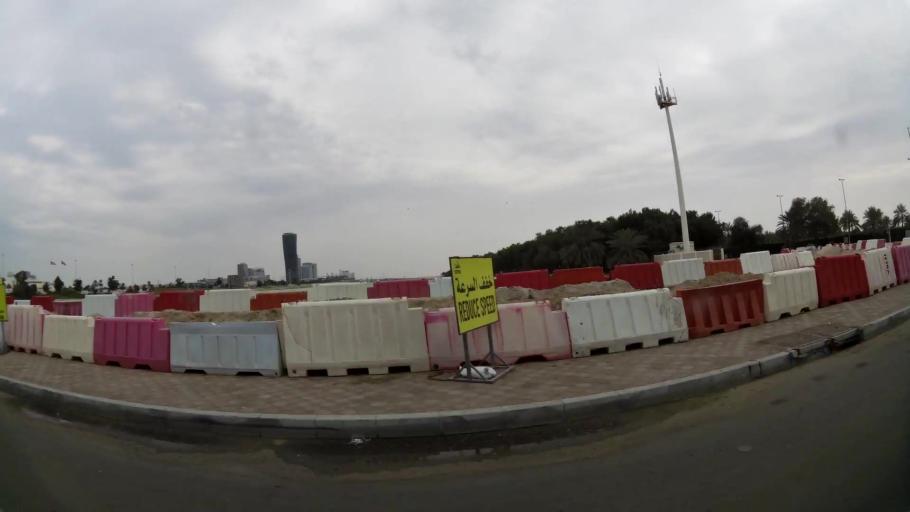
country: AE
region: Abu Dhabi
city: Abu Dhabi
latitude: 24.4188
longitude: 54.4204
